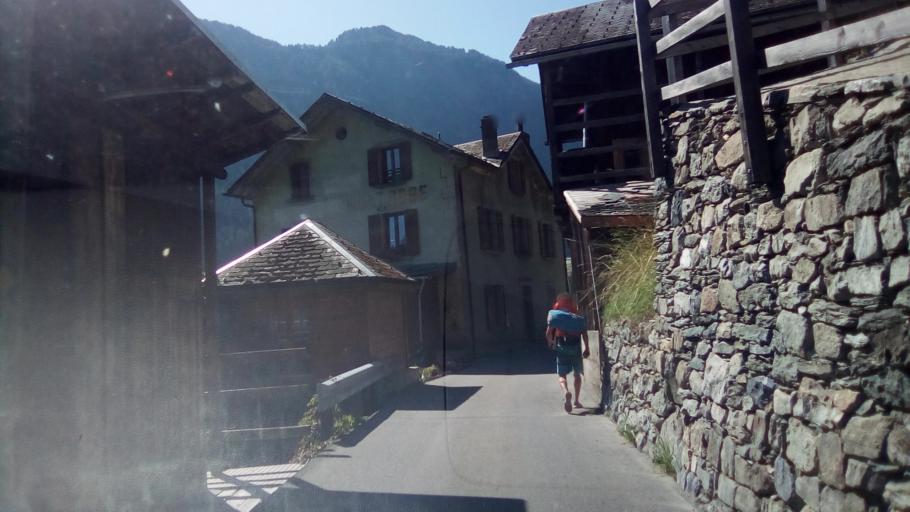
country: CH
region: Valais
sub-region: Saint-Maurice District
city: Salvan
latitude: 46.1028
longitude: 6.9994
